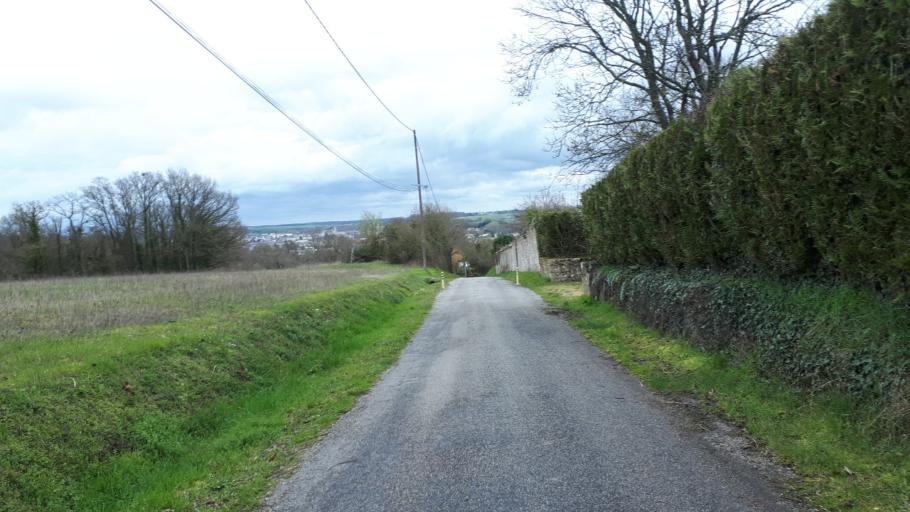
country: FR
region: Centre
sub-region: Departement du Loir-et-Cher
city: Naveil
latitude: 47.8070
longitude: 1.0316
